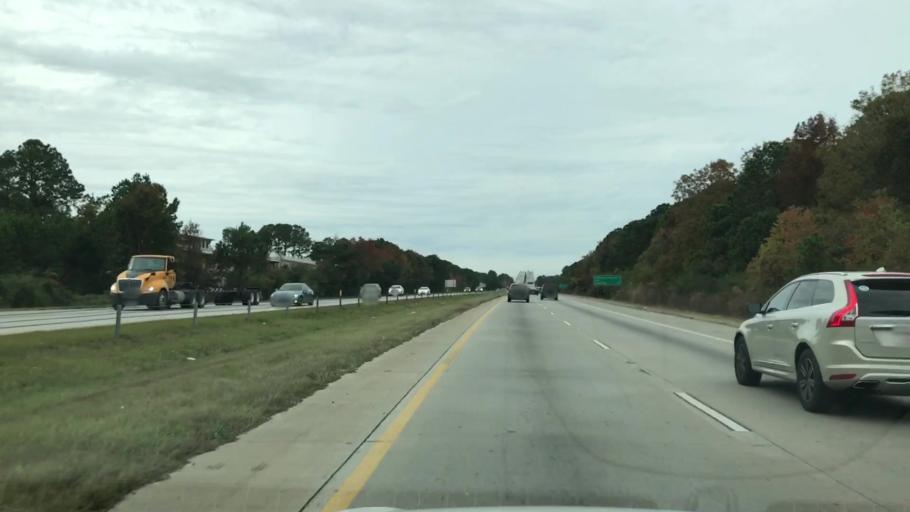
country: US
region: South Carolina
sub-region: Charleston County
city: Mount Pleasant
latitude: 32.8464
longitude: -79.8752
